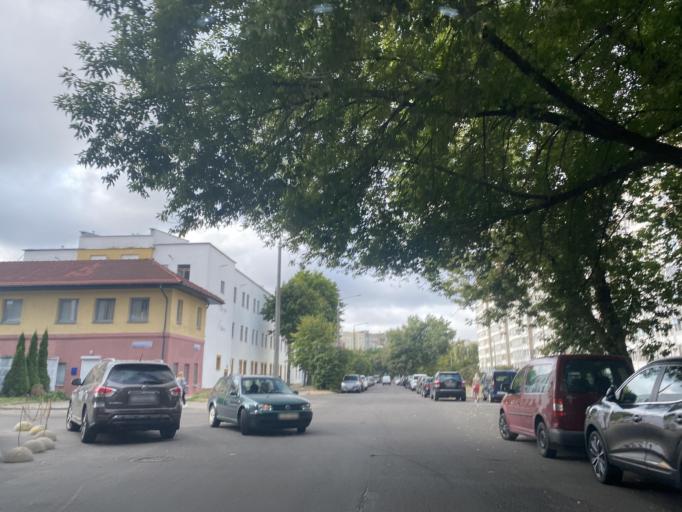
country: BY
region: Minsk
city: Minsk
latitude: 53.9215
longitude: 27.5631
